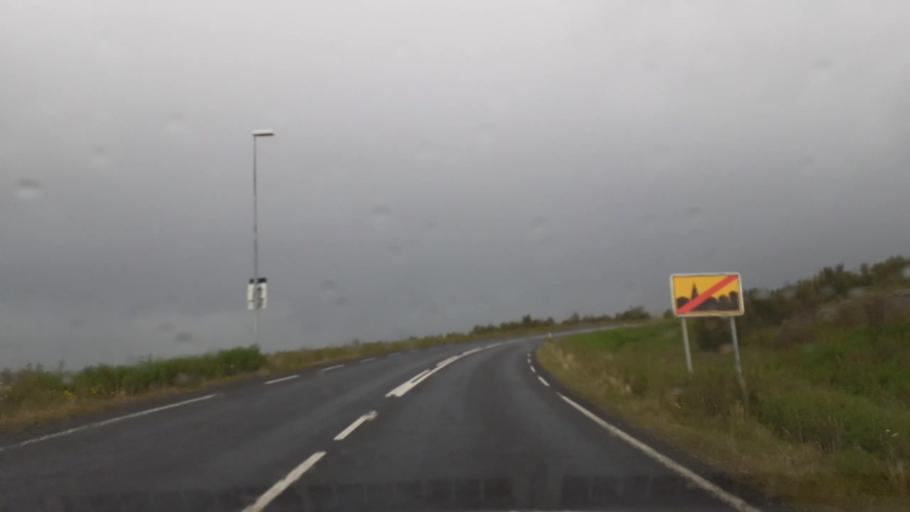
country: IS
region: East
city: Egilsstadir
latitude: 65.2662
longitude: -14.3798
